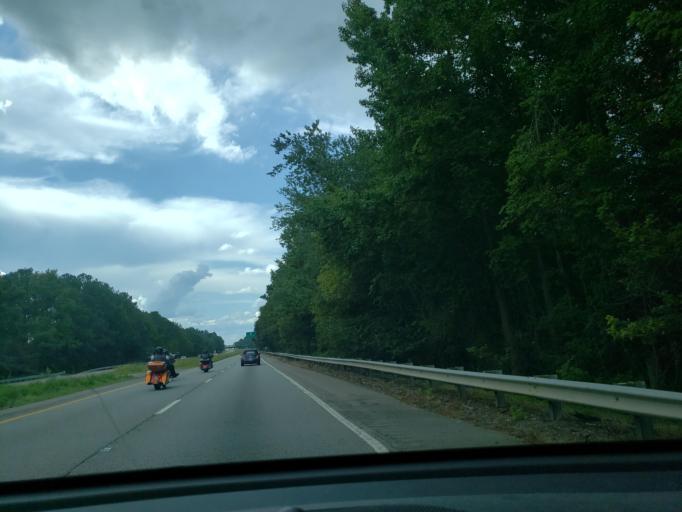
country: US
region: Virginia
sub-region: City of Franklin
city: Franklin
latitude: 36.6412
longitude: -76.8993
